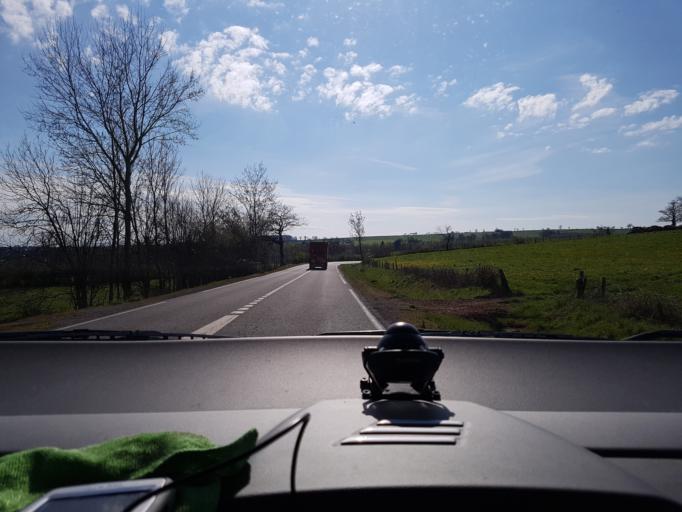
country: FR
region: Midi-Pyrenees
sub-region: Departement de l'Aveyron
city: Moyrazes
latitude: 44.3795
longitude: 2.4550
